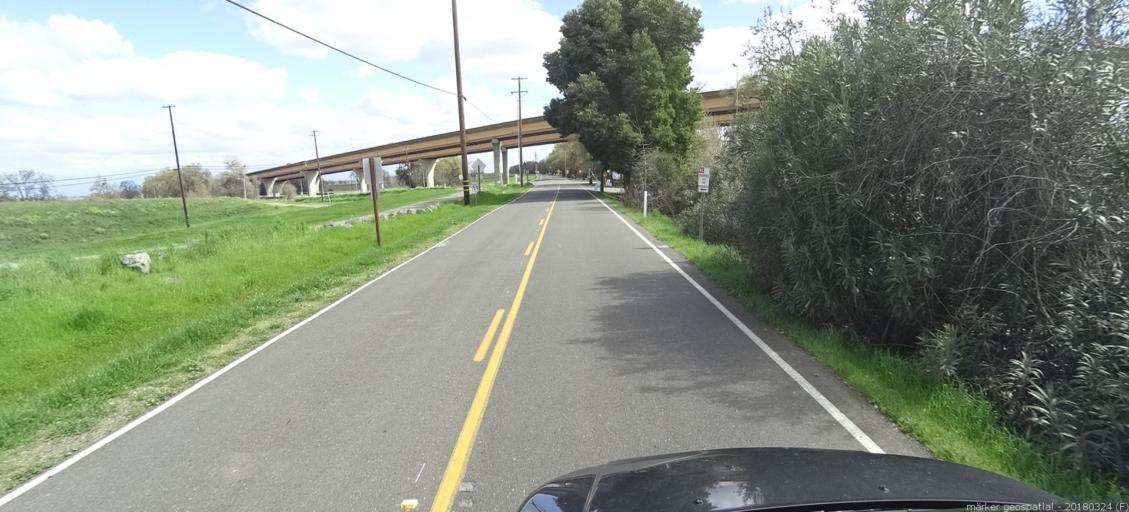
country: US
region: California
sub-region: Yolo County
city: West Sacramento
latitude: 38.6745
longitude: -121.6256
